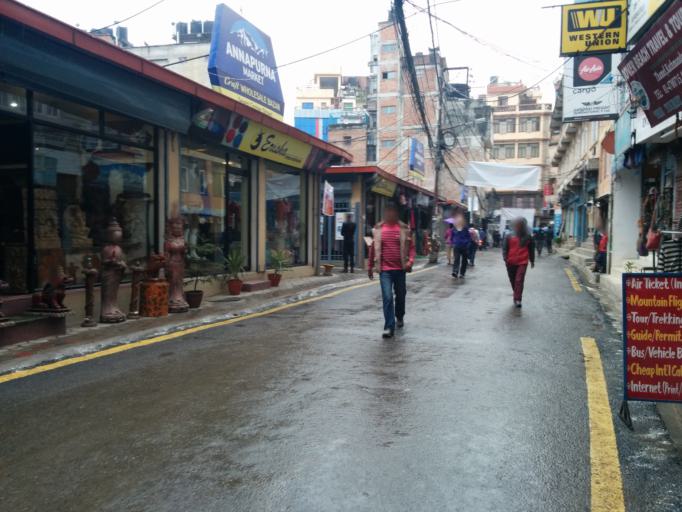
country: NP
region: Central Region
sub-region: Bagmati Zone
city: Kathmandu
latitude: 27.7154
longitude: 85.3092
